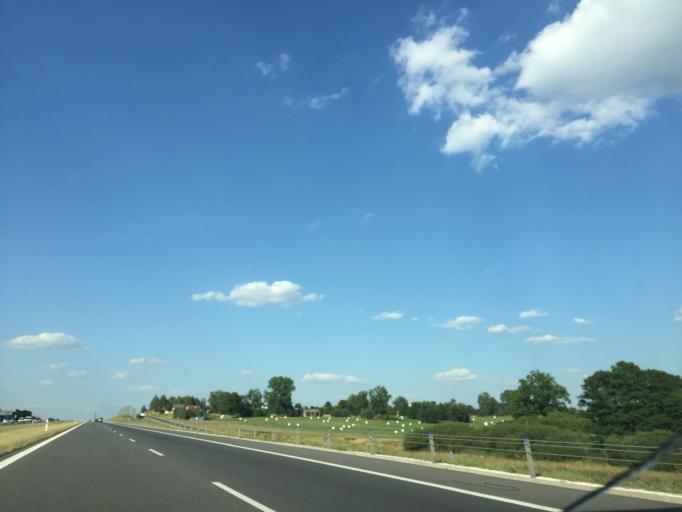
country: PL
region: Swietokrzyskie
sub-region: Powiat kielecki
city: Checiny
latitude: 50.7872
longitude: 20.4733
